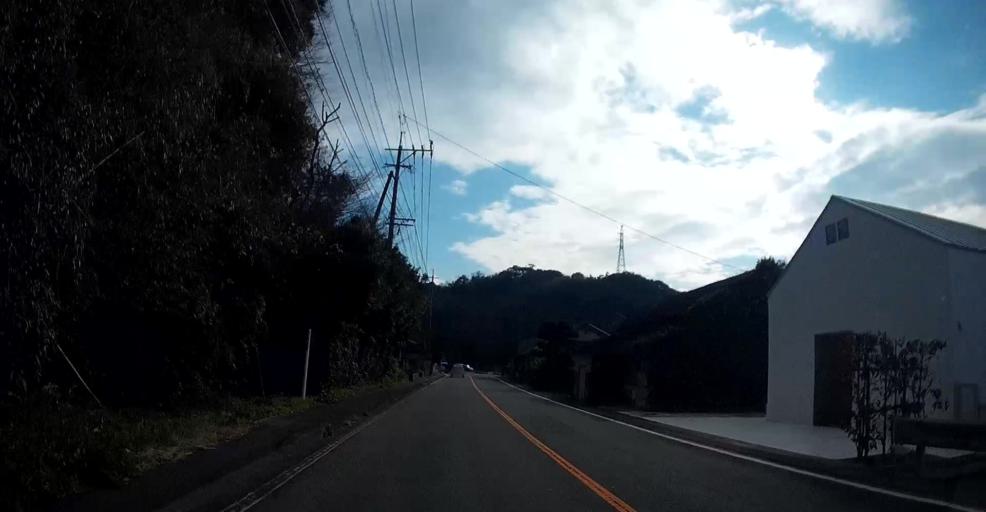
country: JP
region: Kumamoto
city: Yatsushiro
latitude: 32.6142
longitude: 130.4620
